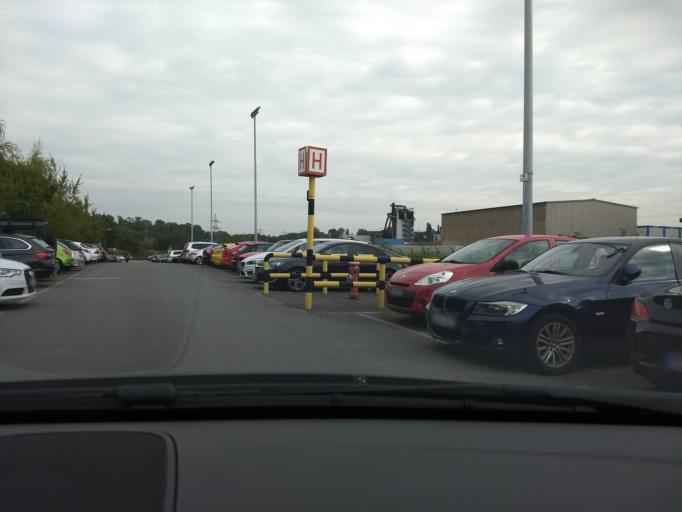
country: DE
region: North Rhine-Westphalia
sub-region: Regierungsbezirk Dusseldorf
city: Essen
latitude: 51.4634
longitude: 7.0296
